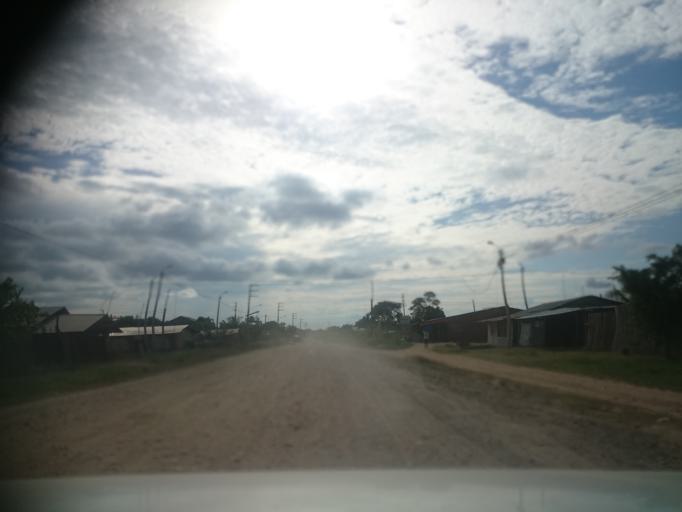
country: PE
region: Ucayali
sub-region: Provincia de Coronel Portillo
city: Puerto Callao
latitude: -8.3709
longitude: -74.5930
